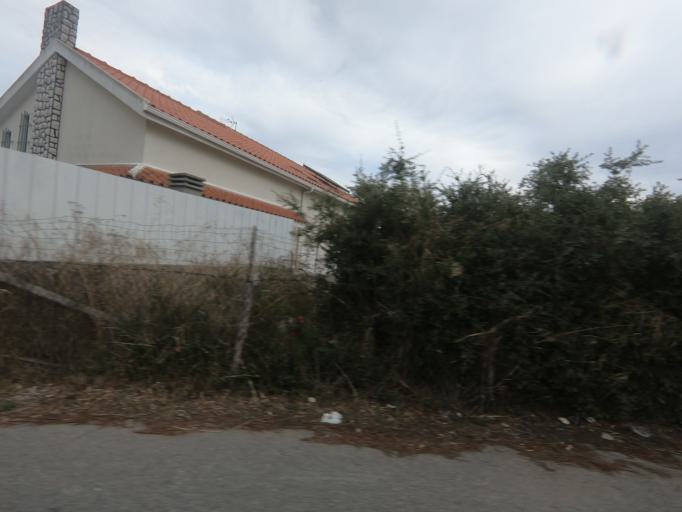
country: PT
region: Setubal
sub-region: Almada
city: Charneca
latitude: 38.6181
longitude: -9.2005
